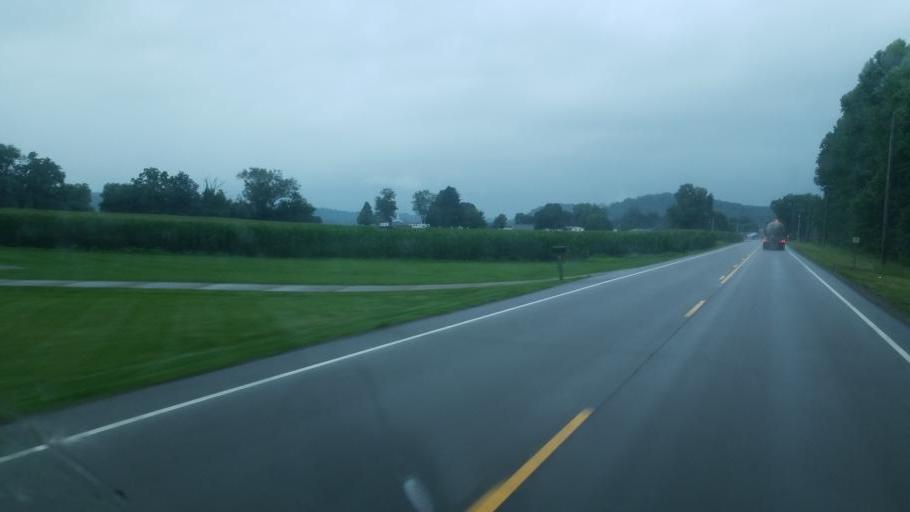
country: US
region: Ohio
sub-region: Coshocton County
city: Coshocton
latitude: 40.3045
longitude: -81.9202
